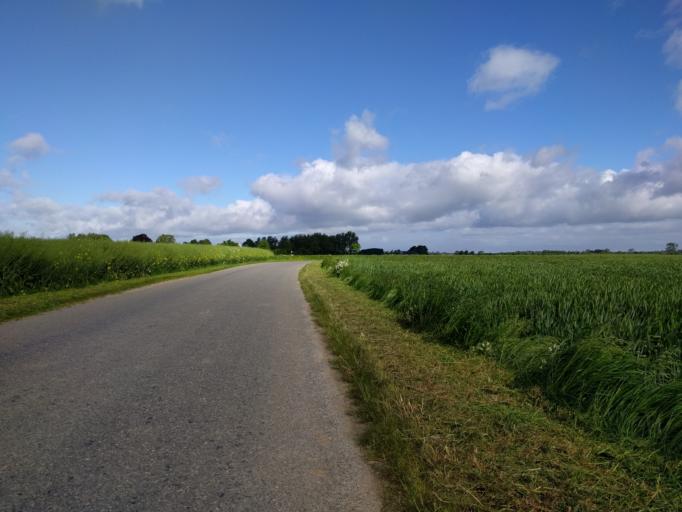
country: DK
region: South Denmark
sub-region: Kerteminde Kommune
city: Kerteminde
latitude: 55.4300
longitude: 10.6273
